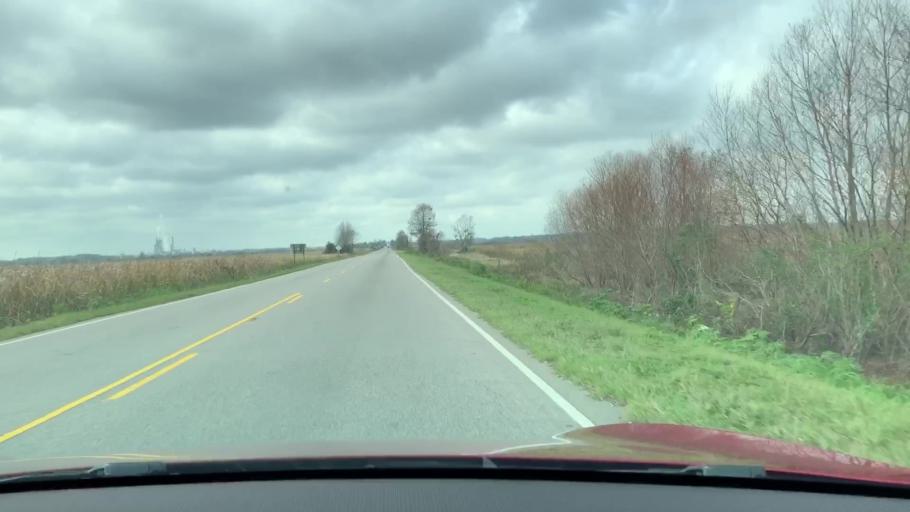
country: US
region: Georgia
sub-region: Chatham County
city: Port Wentworth
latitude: 32.1660
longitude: -81.1174
